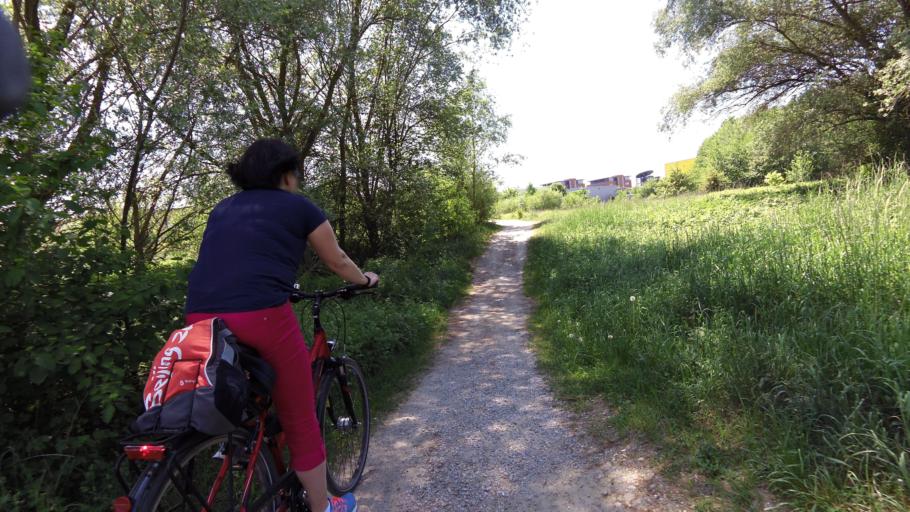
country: DE
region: Bavaria
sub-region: Lower Bavaria
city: Tiefenbach
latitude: 48.5418
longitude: 12.0994
